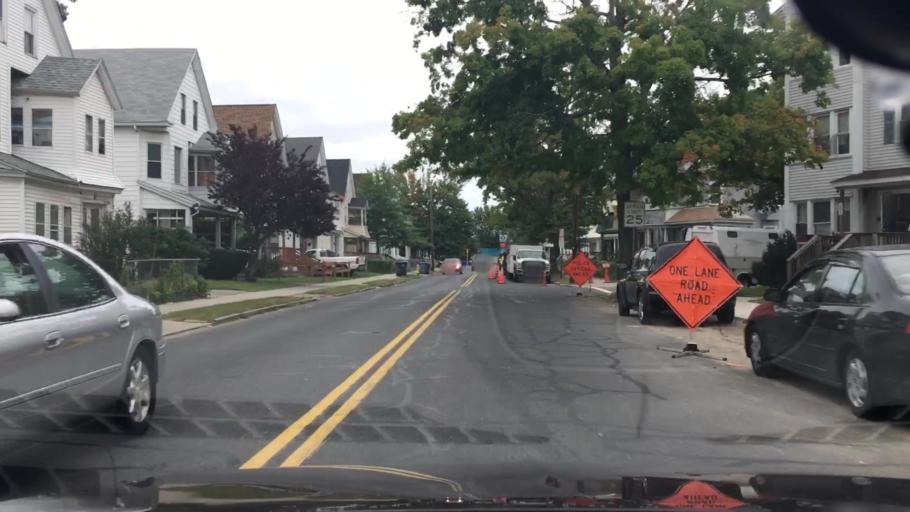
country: US
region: Massachusetts
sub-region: Hampden County
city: Springfield
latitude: 42.0901
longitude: -72.5635
